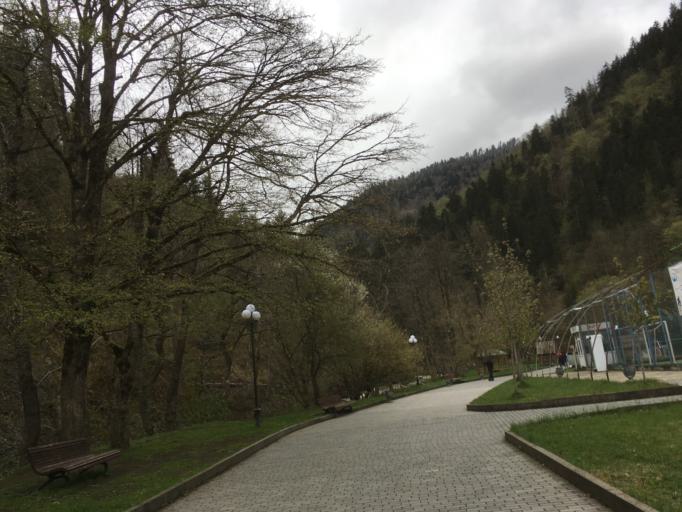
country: GE
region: Samtskhe-Javakheti
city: Borjomi
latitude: 41.8298
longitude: 43.3935
